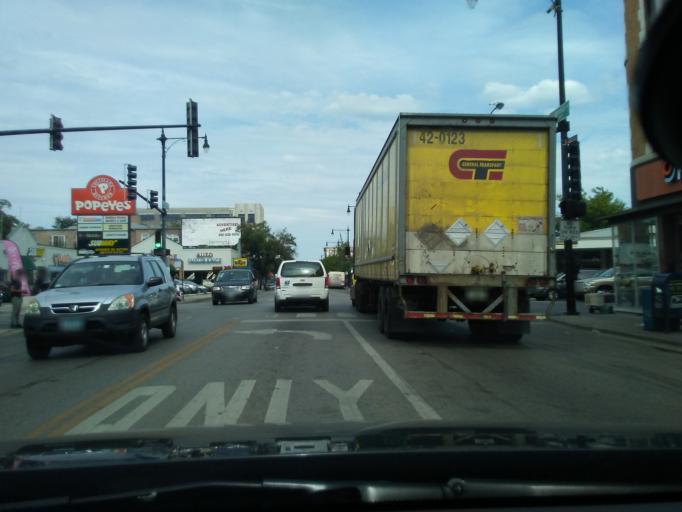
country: US
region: Illinois
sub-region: Cook County
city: Lincolnwood
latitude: 41.9684
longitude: -87.7138
